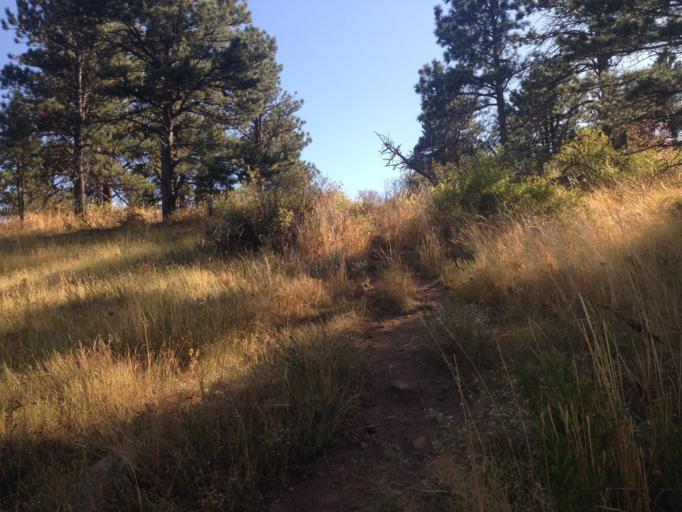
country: US
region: Colorado
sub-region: Boulder County
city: Boulder
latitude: 39.9678
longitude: -105.2635
